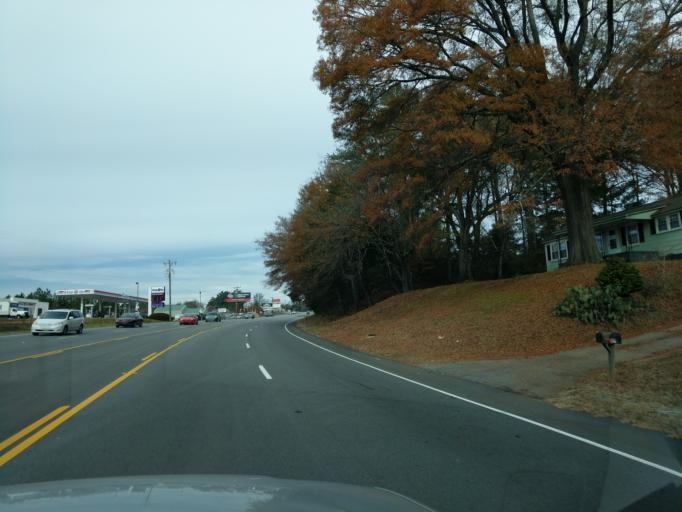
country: US
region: South Carolina
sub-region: Anderson County
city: Pendleton
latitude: 34.6058
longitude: -82.7644
